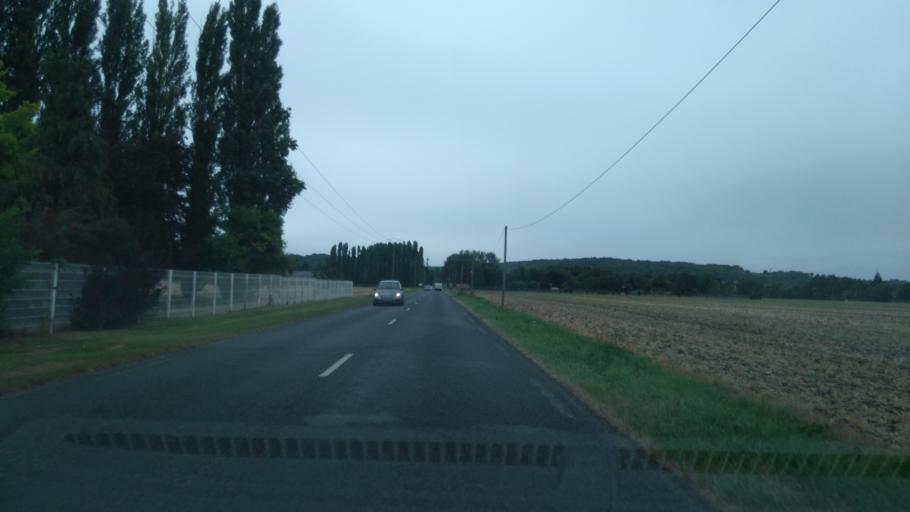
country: FR
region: Picardie
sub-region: Departement de l'Oise
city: Precy-sur-Oise
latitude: 49.1976
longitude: 2.3795
